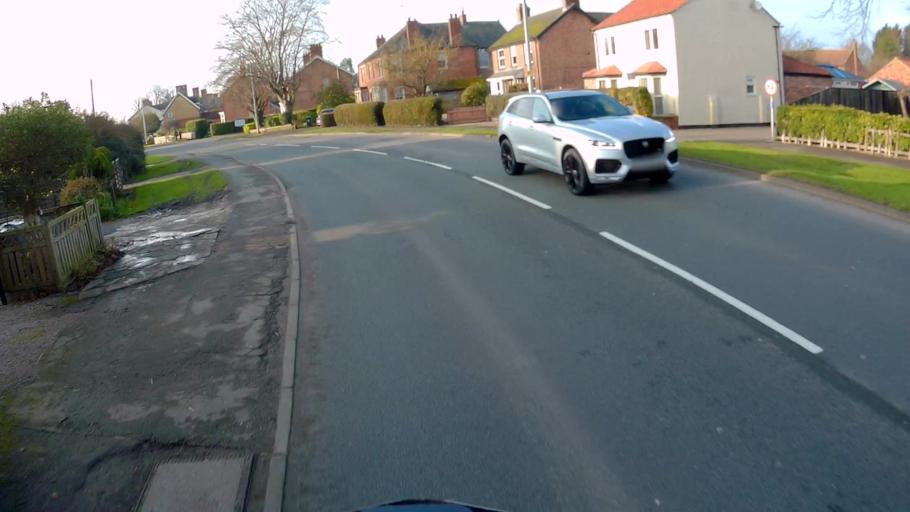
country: GB
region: England
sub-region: Lincolnshire
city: Bourne
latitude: 52.7679
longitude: -0.3855
